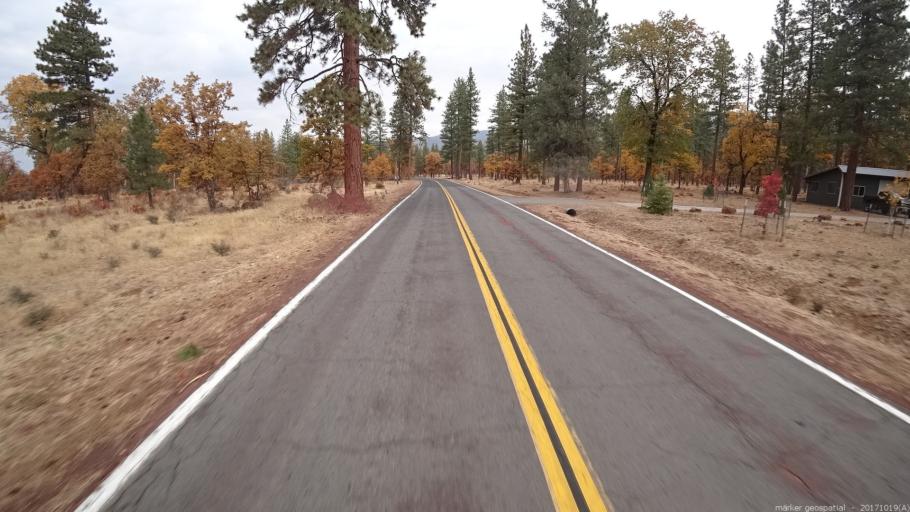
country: US
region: California
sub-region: Shasta County
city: Burney
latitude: 41.1192
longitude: -121.3316
